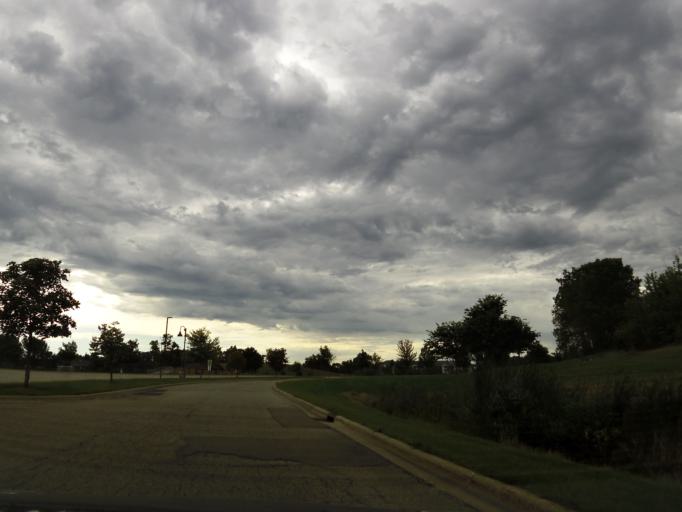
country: US
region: Minnesota
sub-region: Scott County
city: Prior Lake
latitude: 44.7200
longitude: -93.4235
